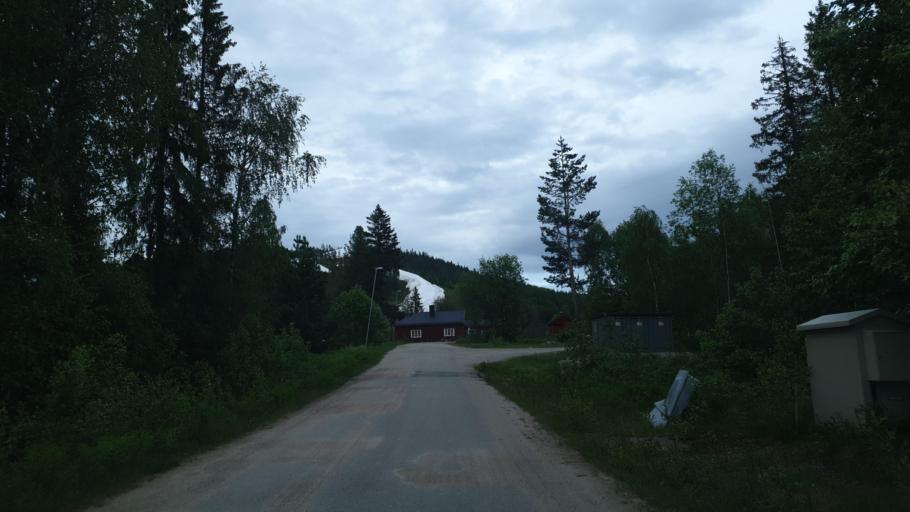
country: SE
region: Norrbotten
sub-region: Jokkmokks Kommun
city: Jokkmokk
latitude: 66.1528
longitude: 19.9848
